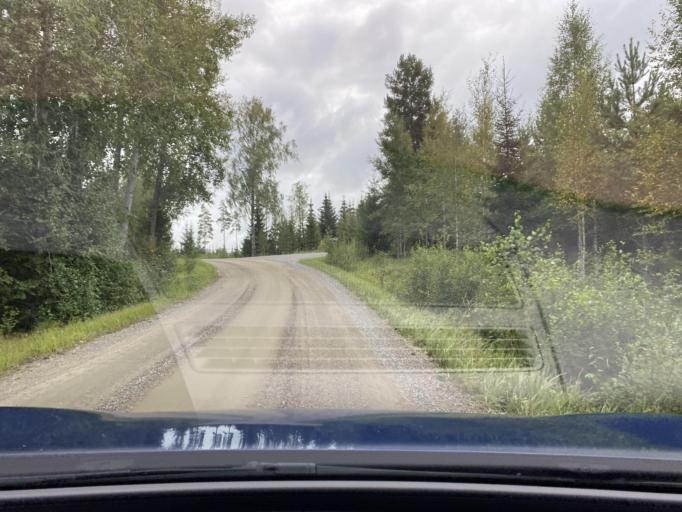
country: FI
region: Pirkanmaa
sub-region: Lounais-Pirkanmaa
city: Punkalaidun
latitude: 61.2121
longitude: 23.1693
